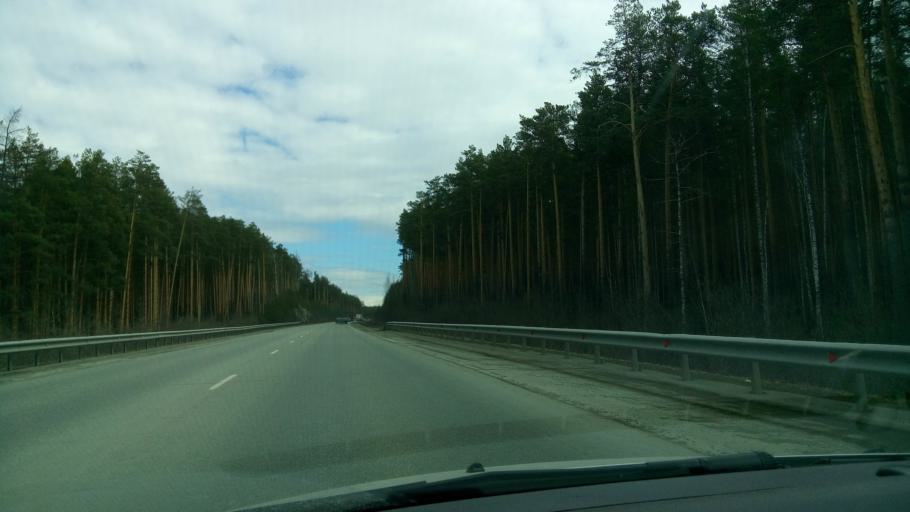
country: RU
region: Sverdlovsk
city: Beryozovsky
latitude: 56.9404
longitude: 60.7063
